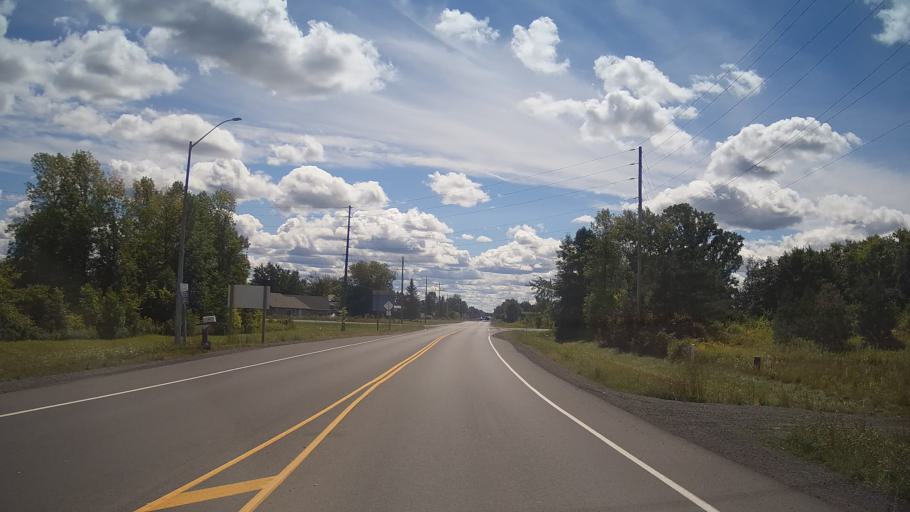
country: US
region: New York
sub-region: St. Lawrence County
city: Ogdensburg
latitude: 44.8460
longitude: -75.3229
